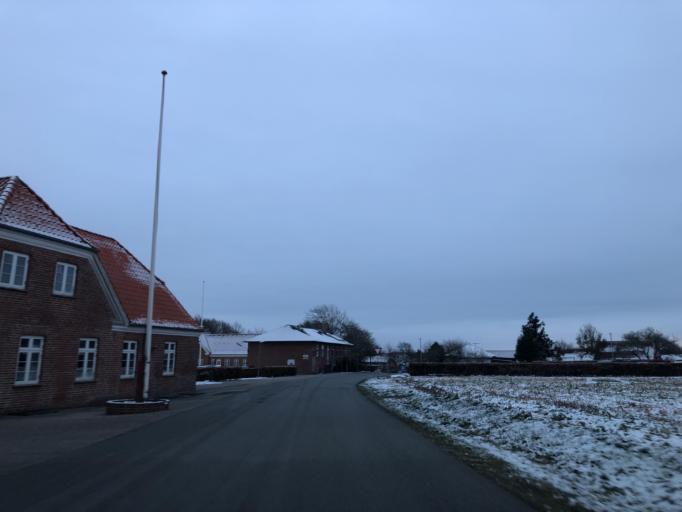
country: DK
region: Central Jutland
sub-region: Holstebro Kommune
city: Ulfborg
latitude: 56.1444
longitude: 8.4302
